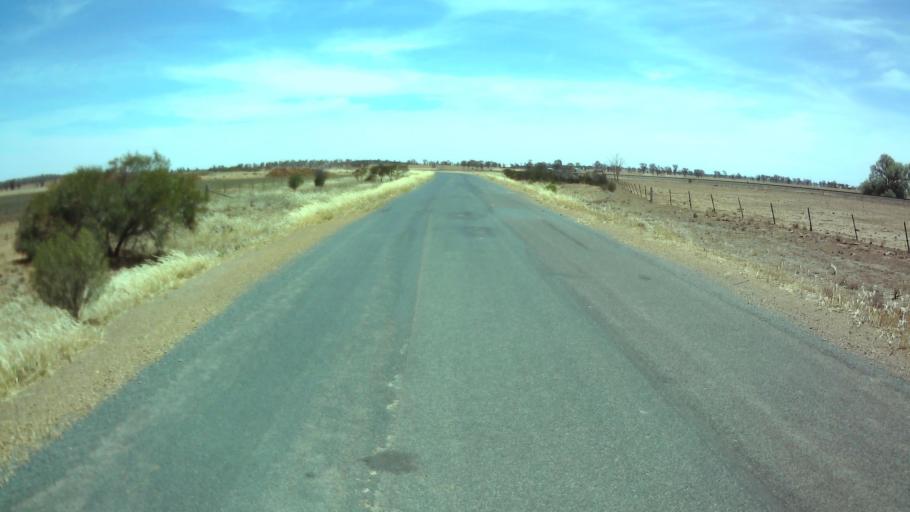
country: AU
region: New South Wales
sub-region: Weddin
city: Grenfell
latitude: -33.7531
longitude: 147.7652
